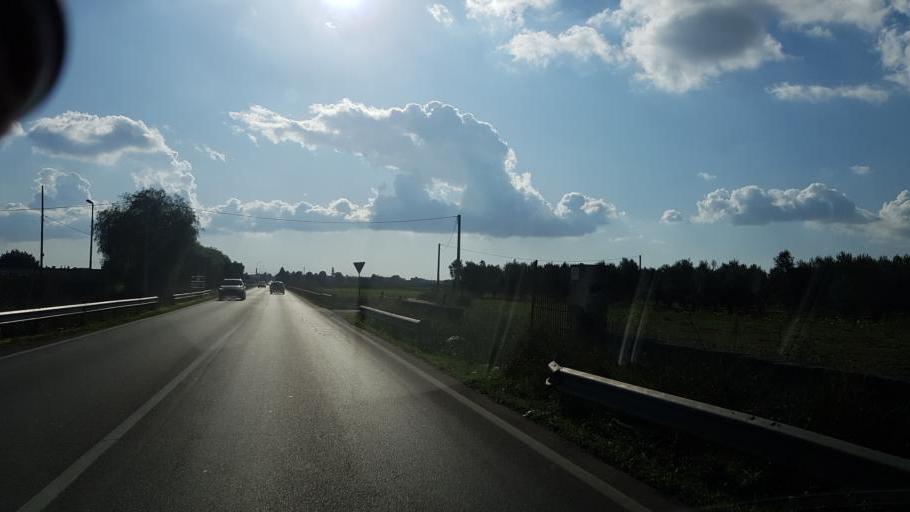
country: IT
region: Apulia
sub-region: Provincia di Lecce
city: Salice Salentino
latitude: 40.3997
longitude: 17.9711
